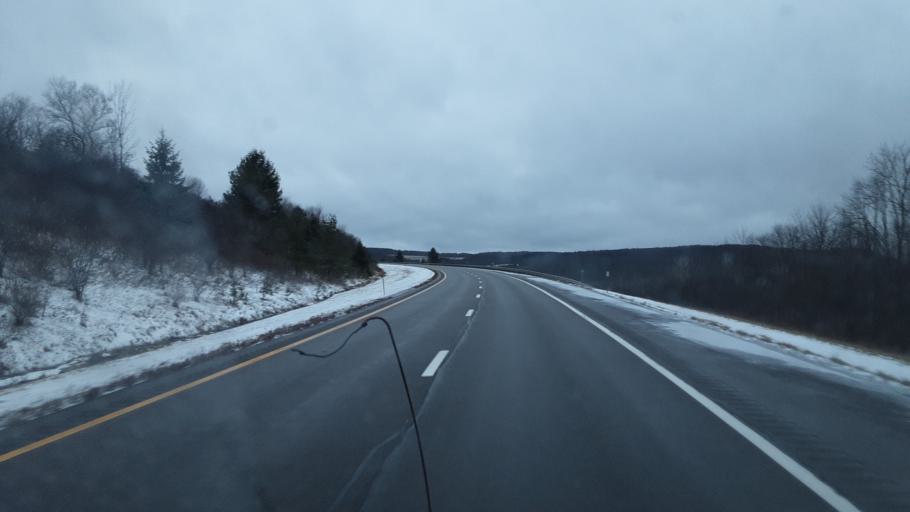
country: US
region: New York
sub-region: Allegany County
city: Alfred
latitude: 42.3202
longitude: -77.8309
